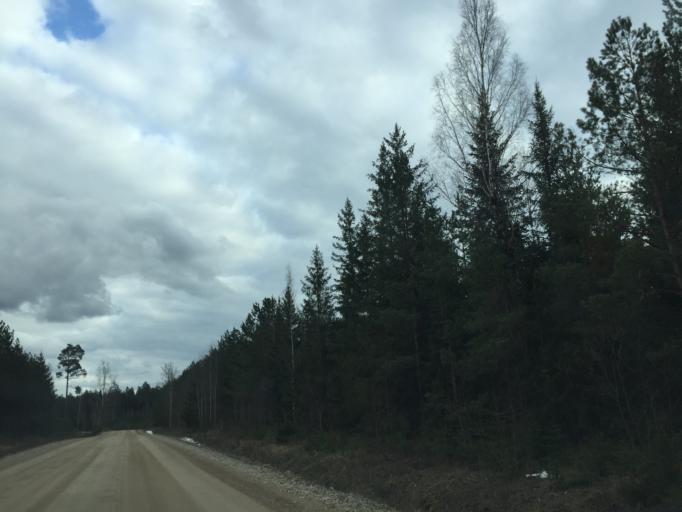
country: LV
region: Ogre
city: Jumprava
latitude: 56.5886
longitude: 24.9930
